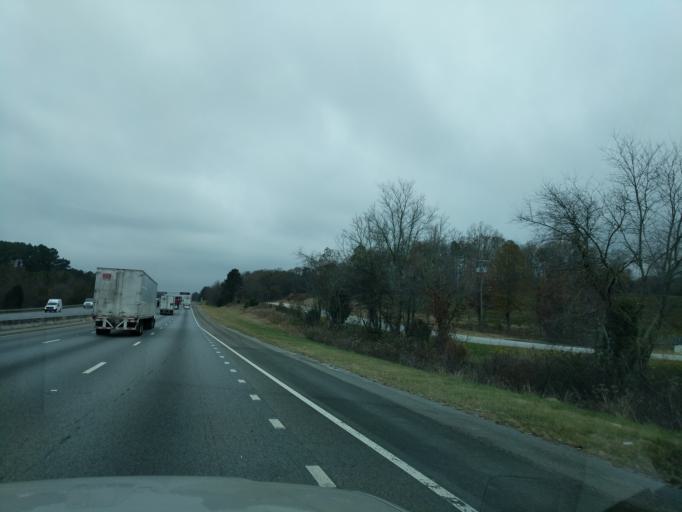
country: US
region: South Carolina
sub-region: Anderson County
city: Powdersville
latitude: 34.7573
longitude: -82.4760
